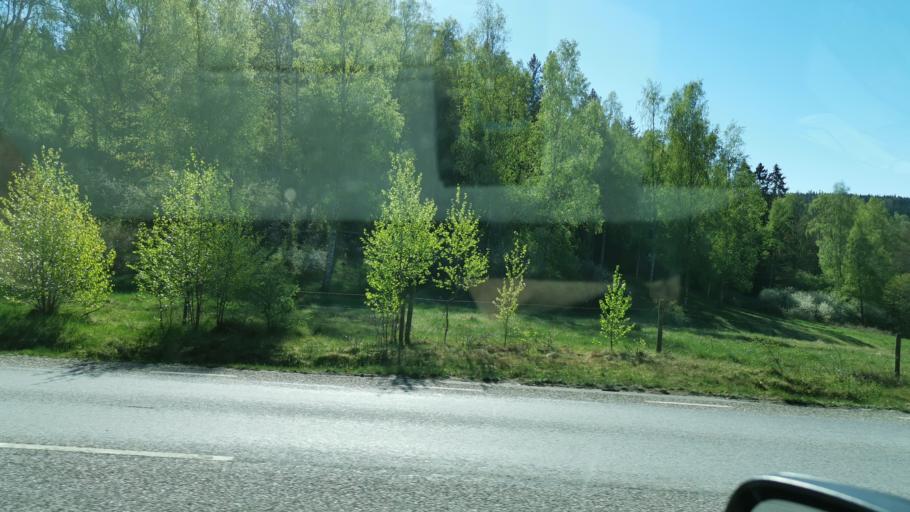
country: SE
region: Vaestra Goetaland
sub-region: Uddevalla Kommun
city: Ljungskile
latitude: 58.2869
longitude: 11.8934
